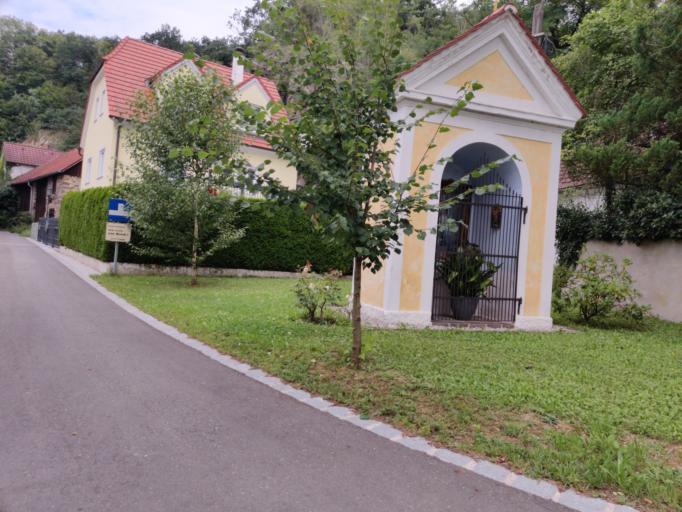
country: AT
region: Lower Austria
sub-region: Politischer Bezirk Melk
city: Leiben
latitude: 48.2302
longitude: 15.2976
